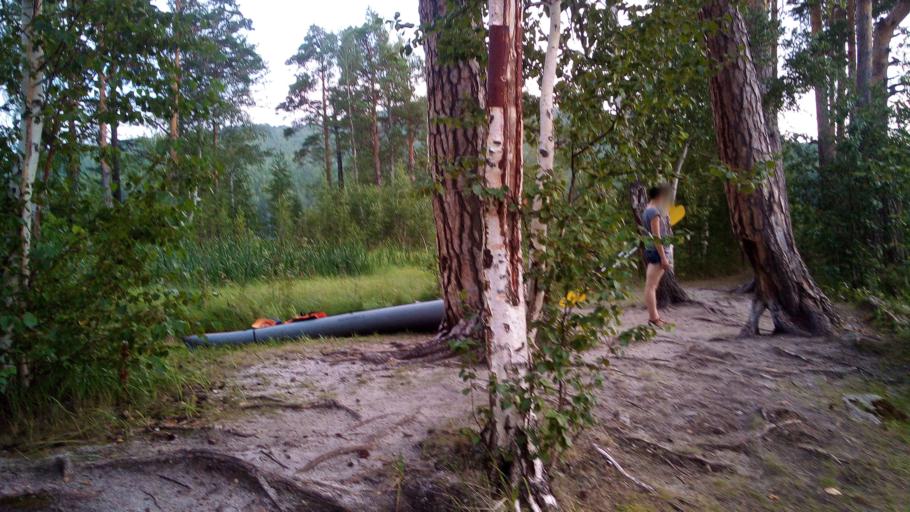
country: RU
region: Chelyabinsk
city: Turgoyak
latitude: 55.1610
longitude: 60.0297
